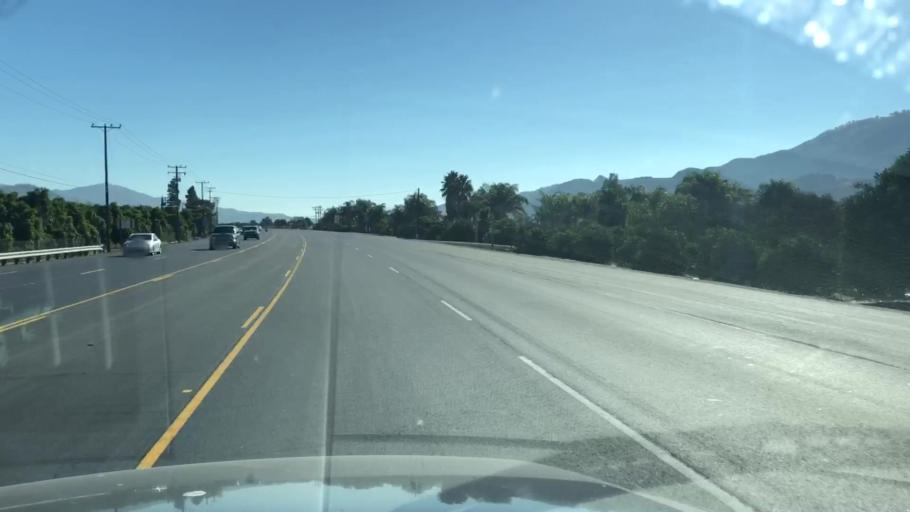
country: US
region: California
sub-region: Ventura County
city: Piru
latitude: 34.4007
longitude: -118.8097
